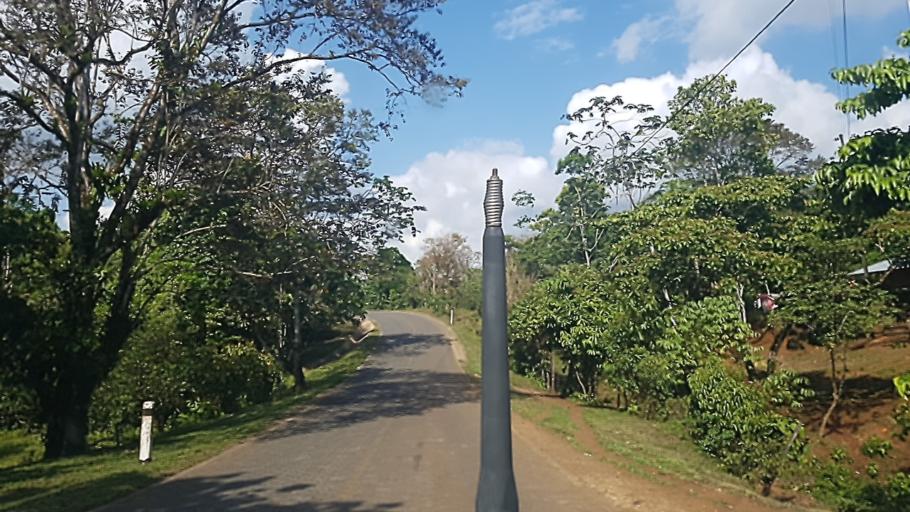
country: NI
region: Atlantico Sur
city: Nueva Guinea
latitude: 11.6976
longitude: -84.3874
